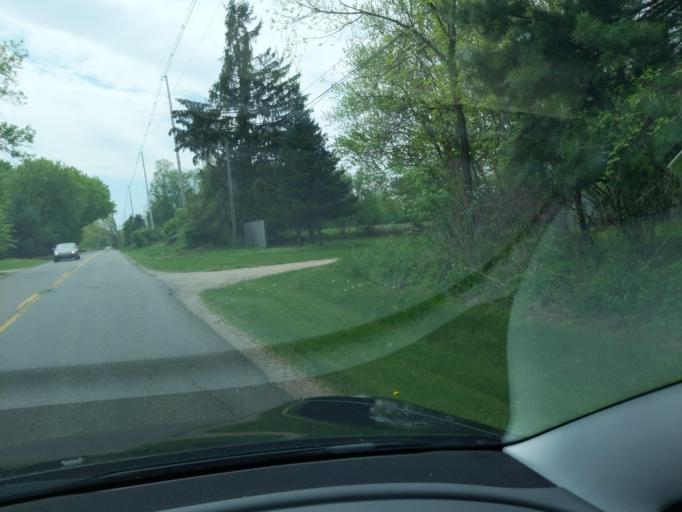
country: US
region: Michigan
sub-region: Ingham County
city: Holt
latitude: 42.6526
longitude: -84.5530
